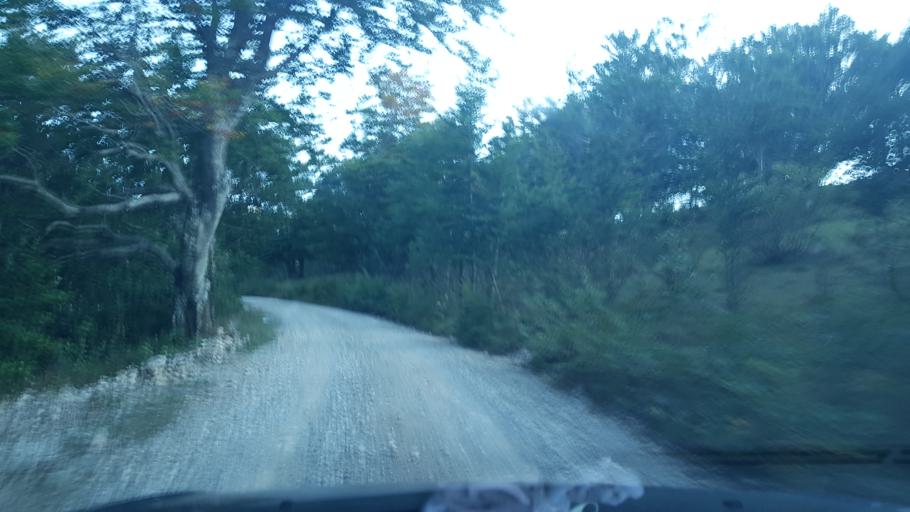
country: SI
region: Vipava
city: Vipava
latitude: 45.7781
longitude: 14.0450
